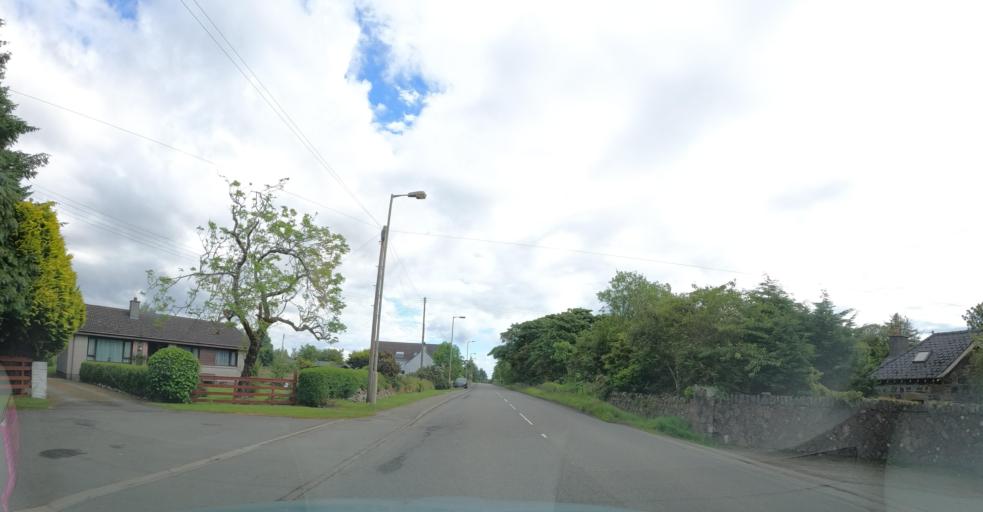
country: GB
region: Scotland
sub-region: Eilean Siar
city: Isle of Lewis
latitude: 58.2167
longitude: -6.4094
